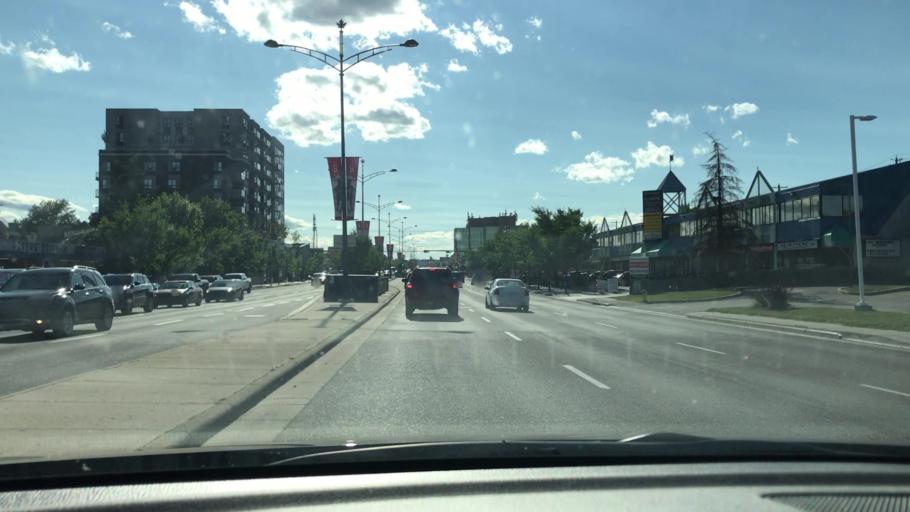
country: CA
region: Alberta
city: Calgary
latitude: 51.0670
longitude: -114.0569
